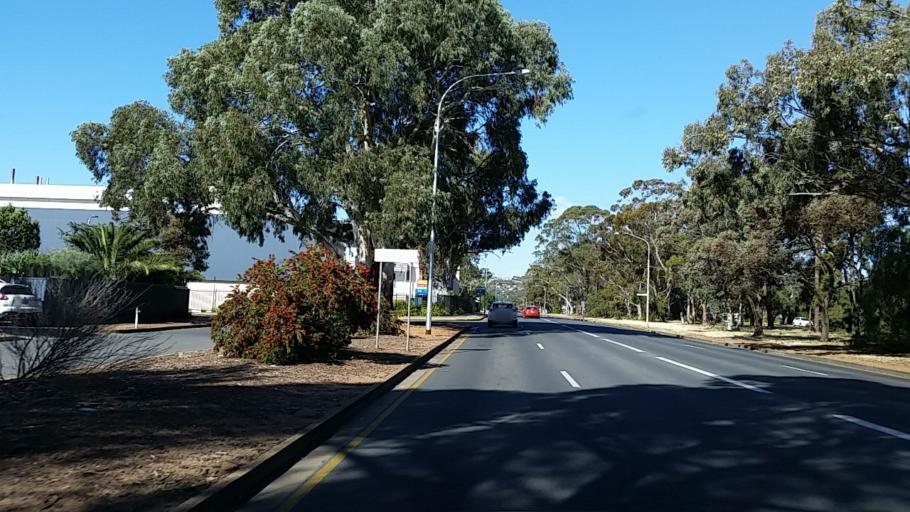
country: AU
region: South Australia
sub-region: Salisbury
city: Elizabeth
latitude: -34.7495
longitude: 138.6644
